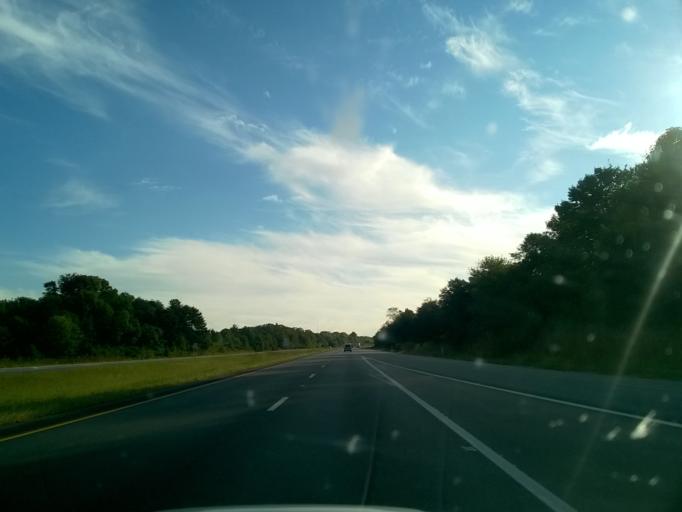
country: US
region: Indiana
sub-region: Warrick County
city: Boonville
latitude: 38.1954
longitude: -87.2897
